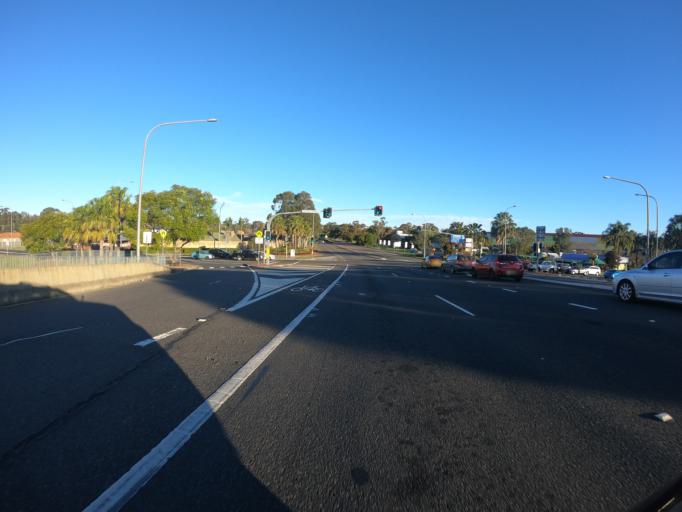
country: AU
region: New South Wales
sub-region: Campbelltown Municipality
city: Leumeah
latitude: -34.0564
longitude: 150.8242
